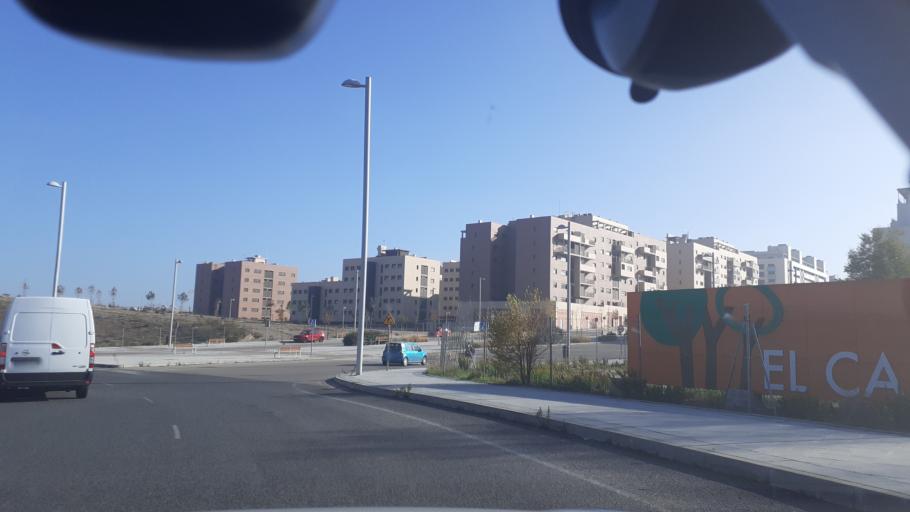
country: ES
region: Madrid
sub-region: Provincia de Madrid
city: Coslada
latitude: 40.4099
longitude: -3.5533
